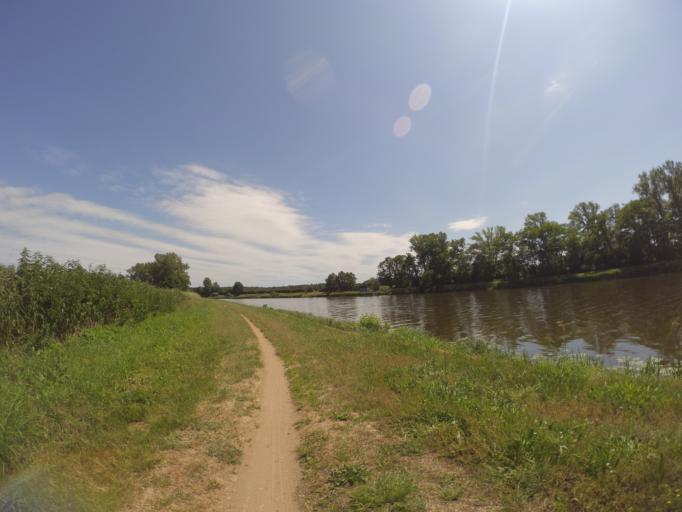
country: CZ
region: Central Bohemia
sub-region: Okres Nymburk
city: Sadska
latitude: 50.1648
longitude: 14.9575
